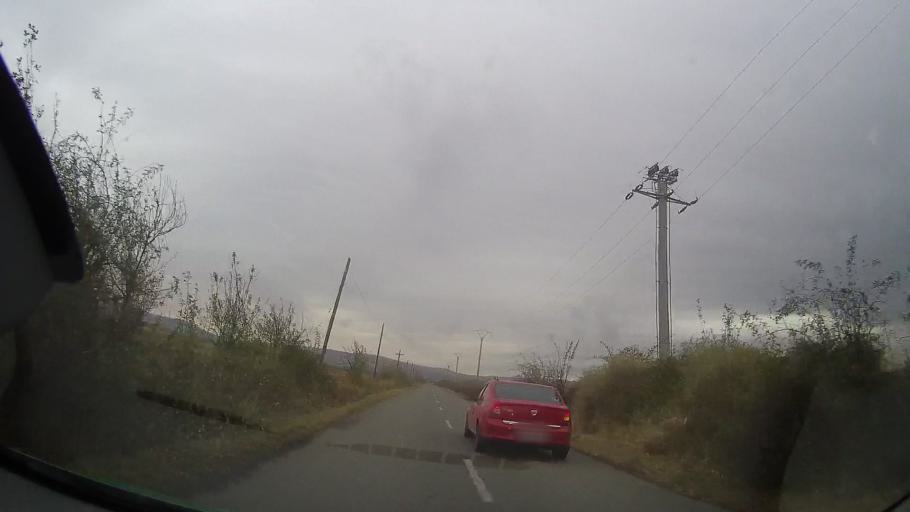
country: RO
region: Prahova
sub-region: Comuna Fantanele
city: Fantanele
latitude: 45.0171
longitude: 26.3803
